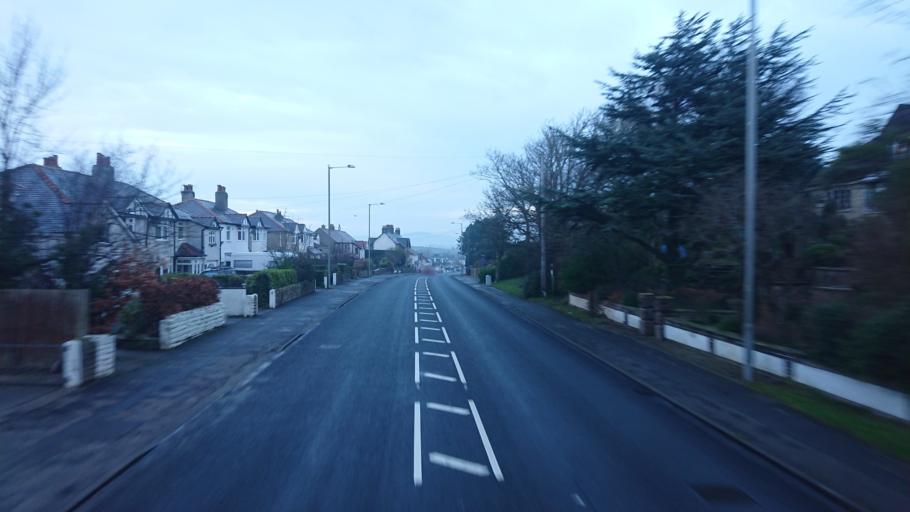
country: GB
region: England
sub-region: Lancashire
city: Bolton le Sands
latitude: 54.0881
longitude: -2.8169
